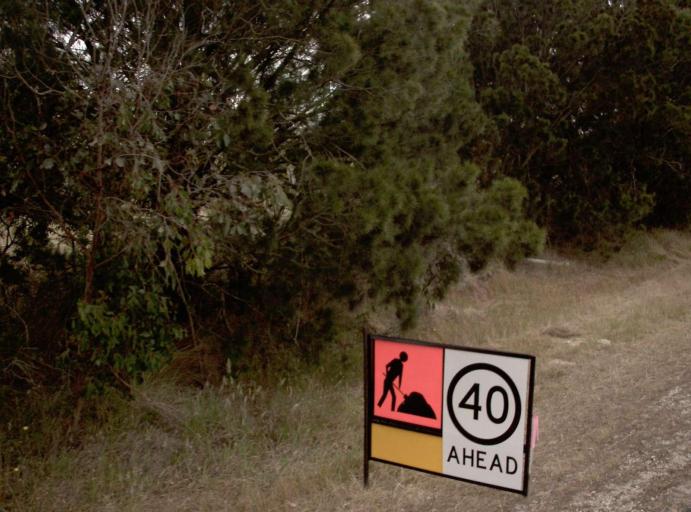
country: AU
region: Victoria
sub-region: Wellington
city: Sale
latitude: -38.1328
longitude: 147.4201
